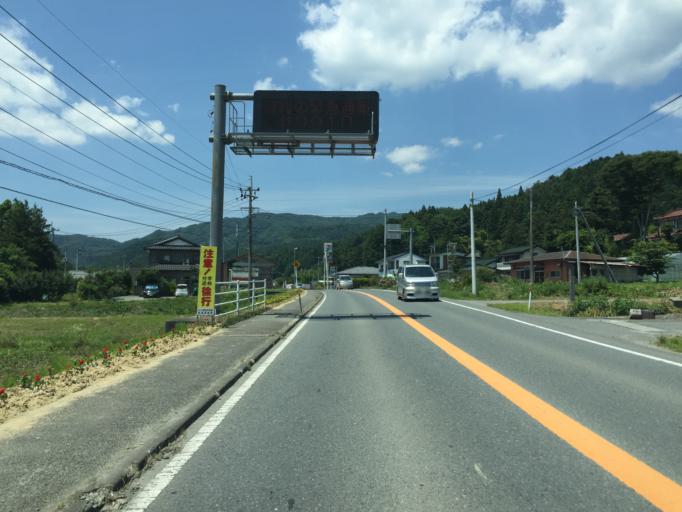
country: JP
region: Miyagi
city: Marumori
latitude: 37.7779
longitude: 140.8819
